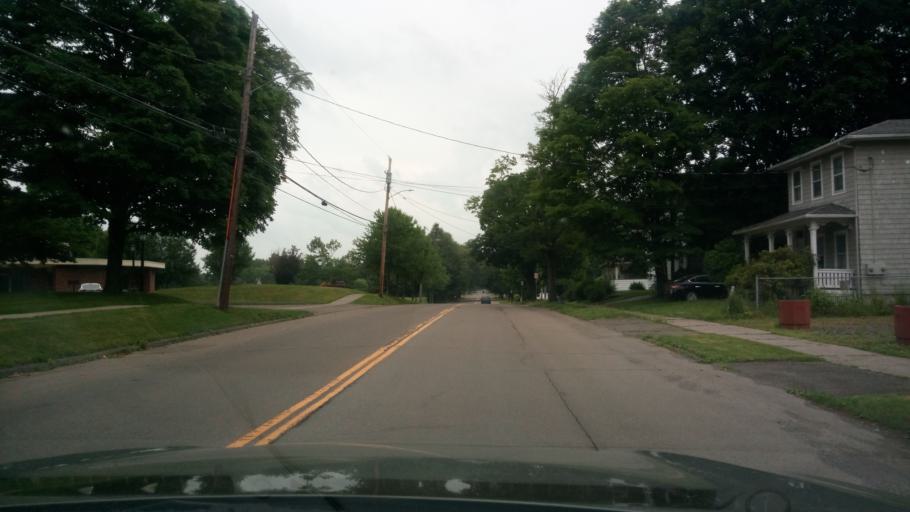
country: US
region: New York
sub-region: Chemung County
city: Elmira
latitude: 42.0964
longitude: -76.8186
